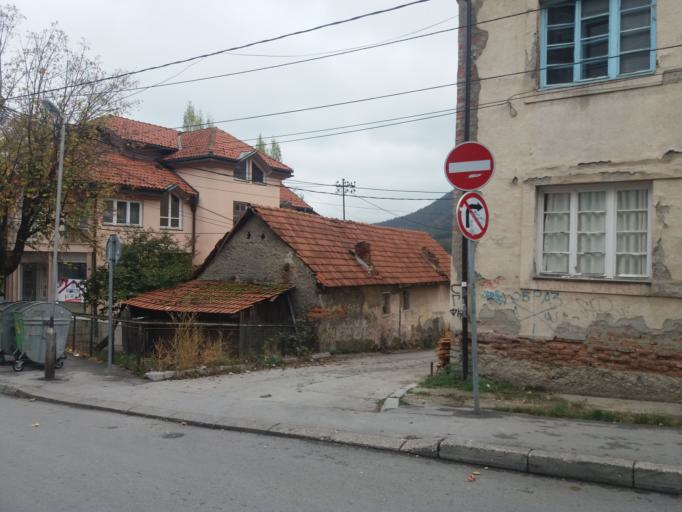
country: RS
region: Central Serbia
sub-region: Zlatiborski Okrug
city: Uzice
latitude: 43.8577
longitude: 19.8360
